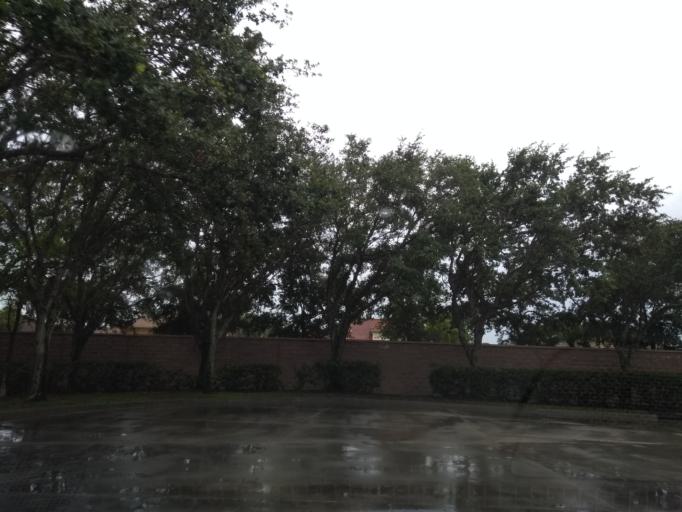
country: US
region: Florida
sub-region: Collier County
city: Pine Ridge
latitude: 26.2071
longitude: -81.7660
